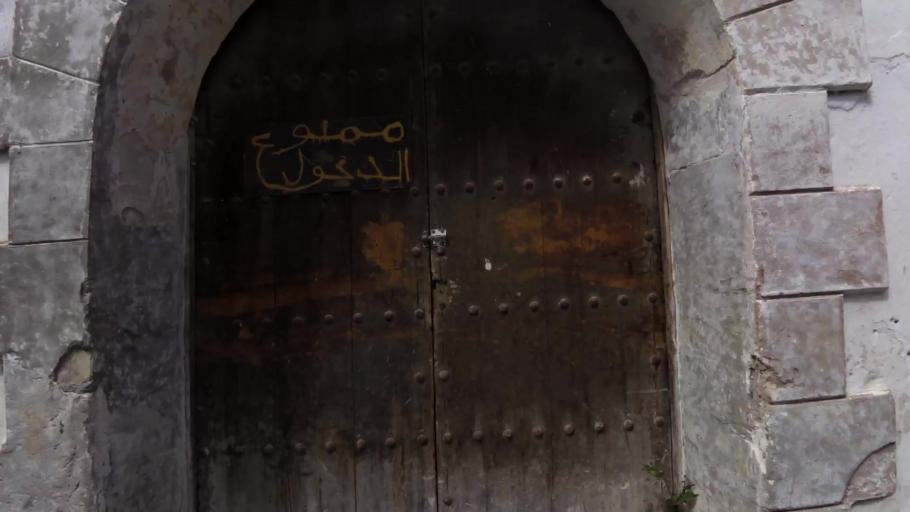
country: MA
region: Tanger-Tetouan
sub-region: Tanger-Assilah
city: Tangier
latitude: 35.7890
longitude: -5.8142
